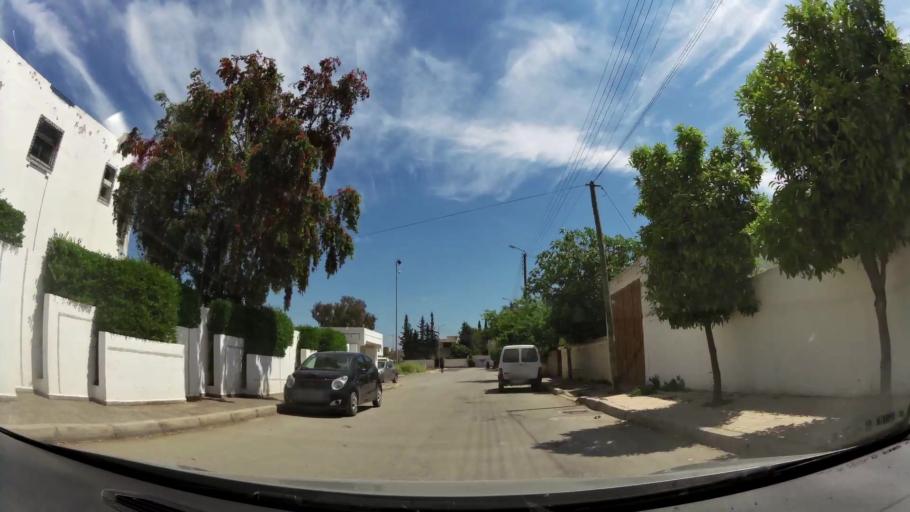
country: MA
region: Fes-Boulemane
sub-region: Fes
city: Fes
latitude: 34.0101
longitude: -4.9933
